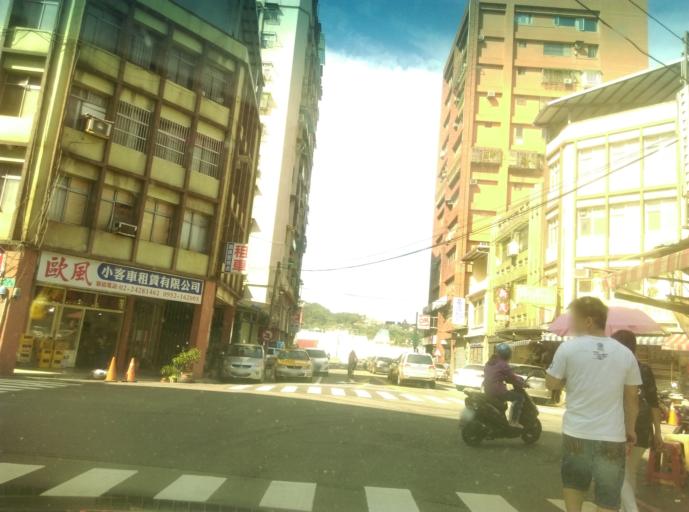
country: TW
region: Taiwan
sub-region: Keelung
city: Keelung
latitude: 25.1377
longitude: 121.7513
